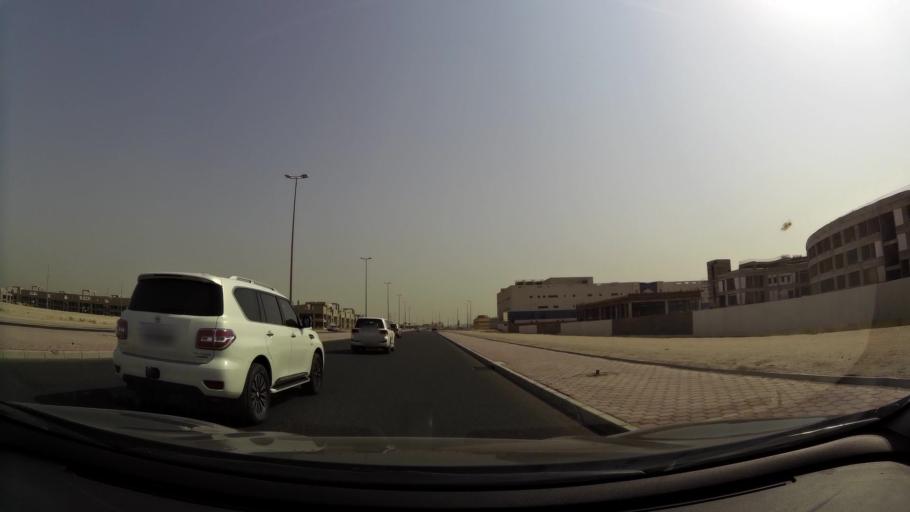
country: KW
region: Al Asimah
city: Ar Rabiyah
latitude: 29.2887
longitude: 47.9090
